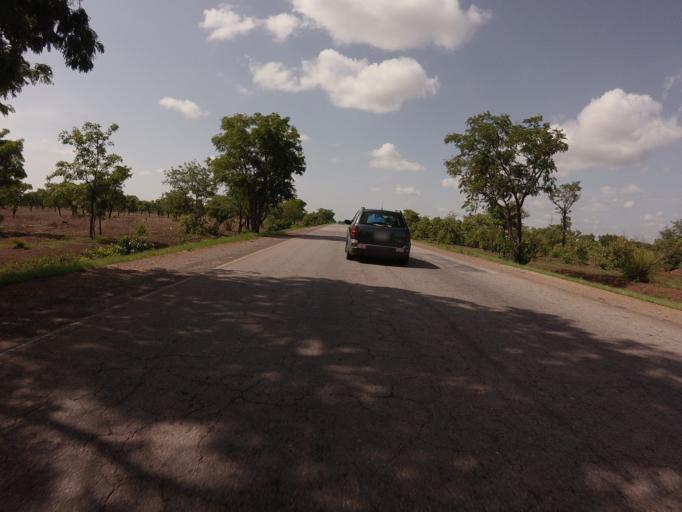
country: GH
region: Northern
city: Savelugu
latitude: 9.9583
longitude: -0.8336
